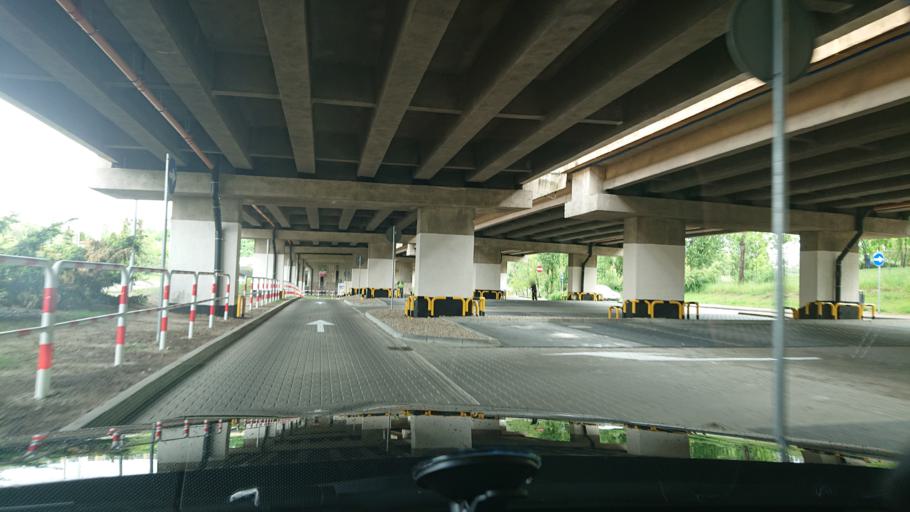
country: PL
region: Greater Poland Voivodeship
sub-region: Powiat gnieznienski
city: Gniezno
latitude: 52.5438
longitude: 17.6039
